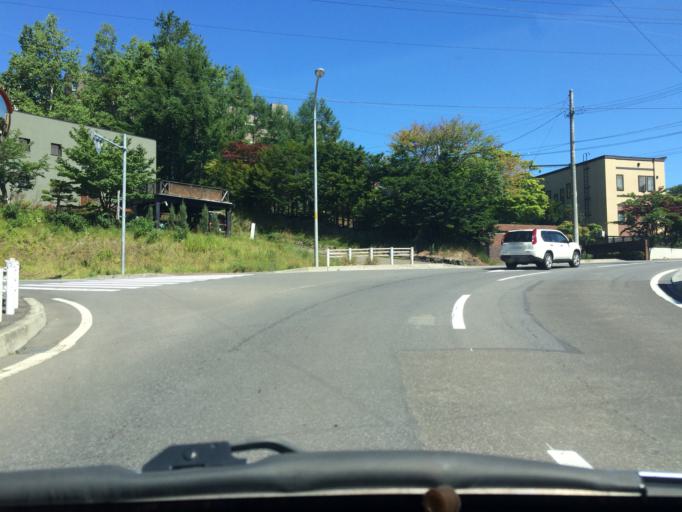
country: JP
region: Hokkaido
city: Sapporo
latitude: 43.0468
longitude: 141.2926
